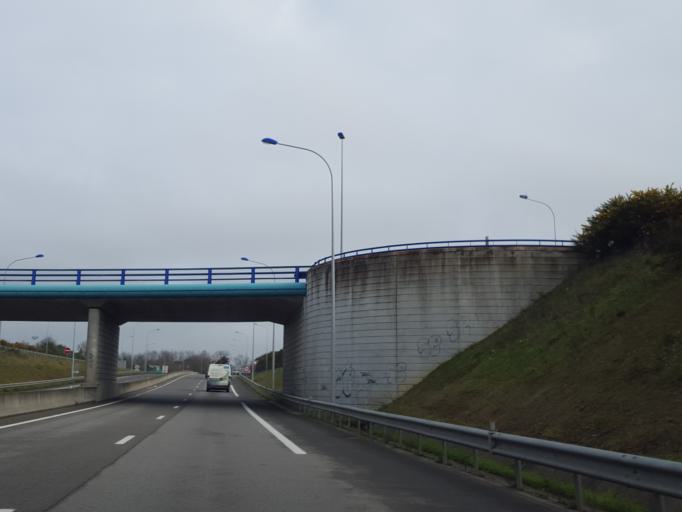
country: FR
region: Pays de la Loire
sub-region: Departement de la Vendee
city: La Roche-sur-Yon
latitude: 46.6837
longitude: -1.4474
